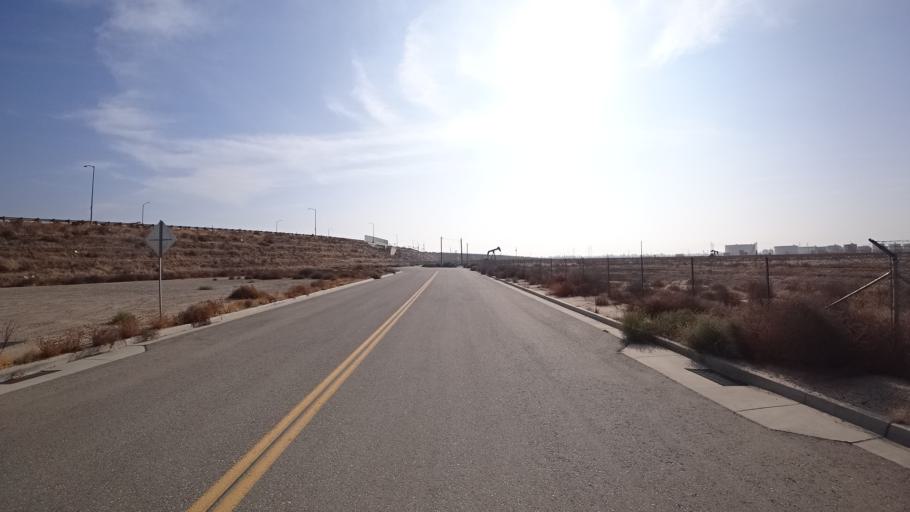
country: US
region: California
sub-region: Kern County
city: Greenacres
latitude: 35.3778
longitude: -119.0666
